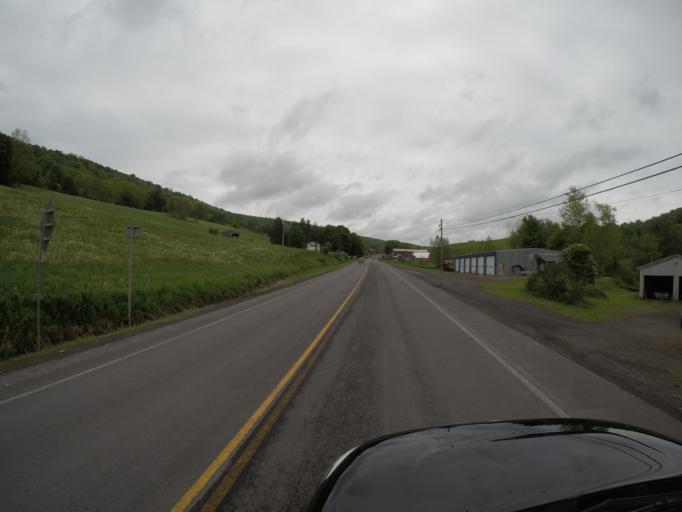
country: US
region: New York
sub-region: Delaware County
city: Delhi
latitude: 42.1979
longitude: -74.7907
